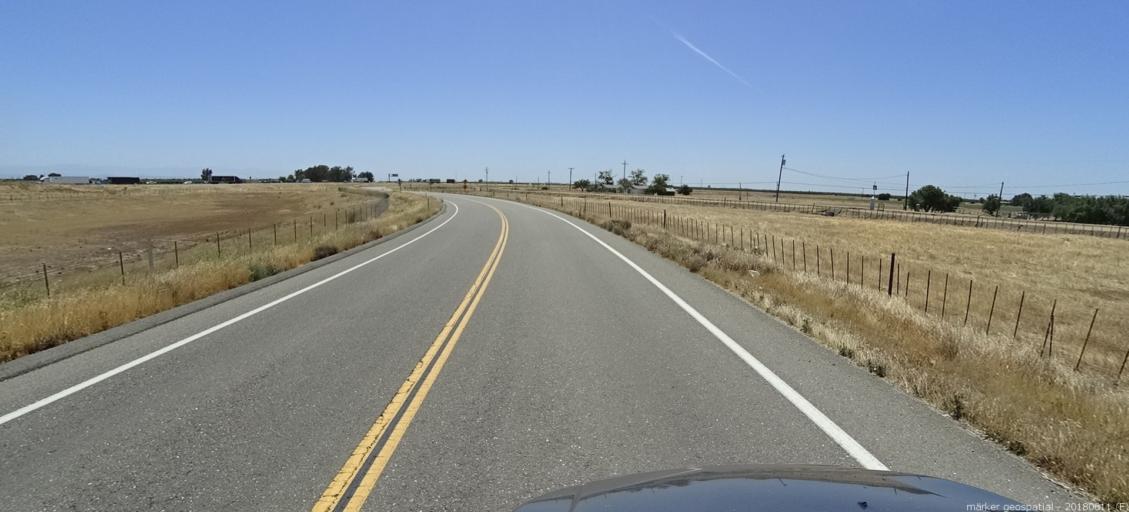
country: US
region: California
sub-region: Madera County
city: Fairmead
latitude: 37.0629
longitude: -120.1873
